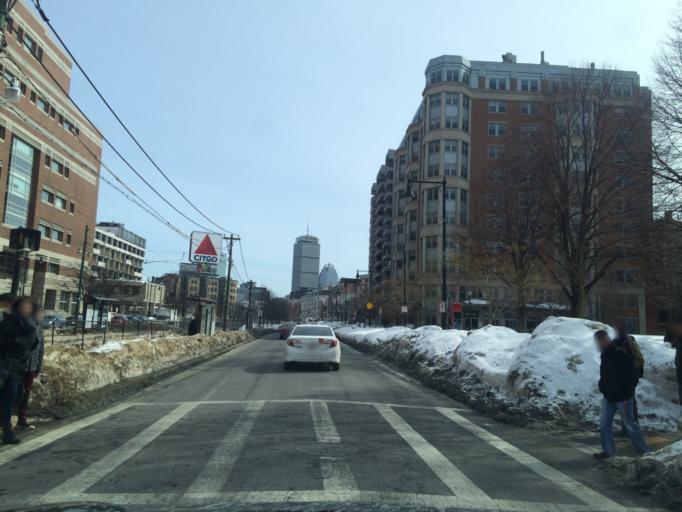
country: US
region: Massachusetts
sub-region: Middlesex County
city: Cambridge
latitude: 42.3492
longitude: -71.1006
